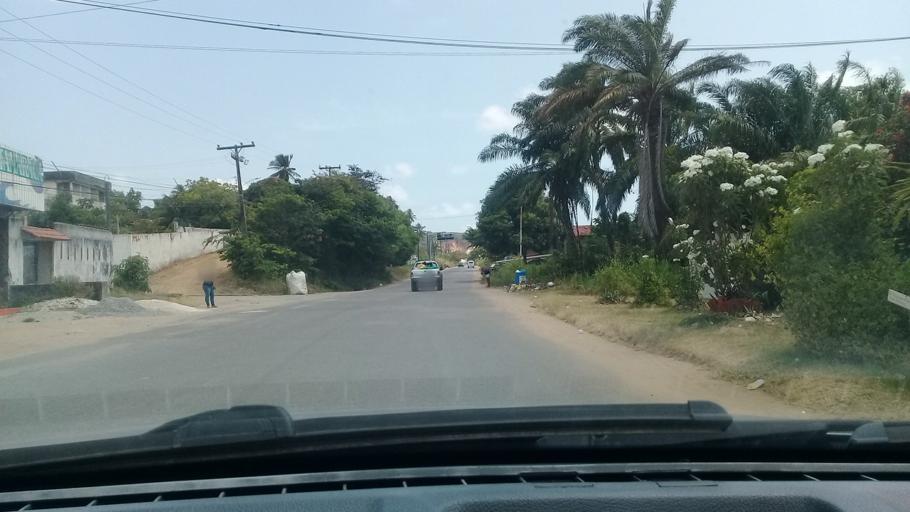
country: BR
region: Pernambuco
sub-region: Itamaraca
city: Itamaraca
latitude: -7.7933
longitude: -34.8418
